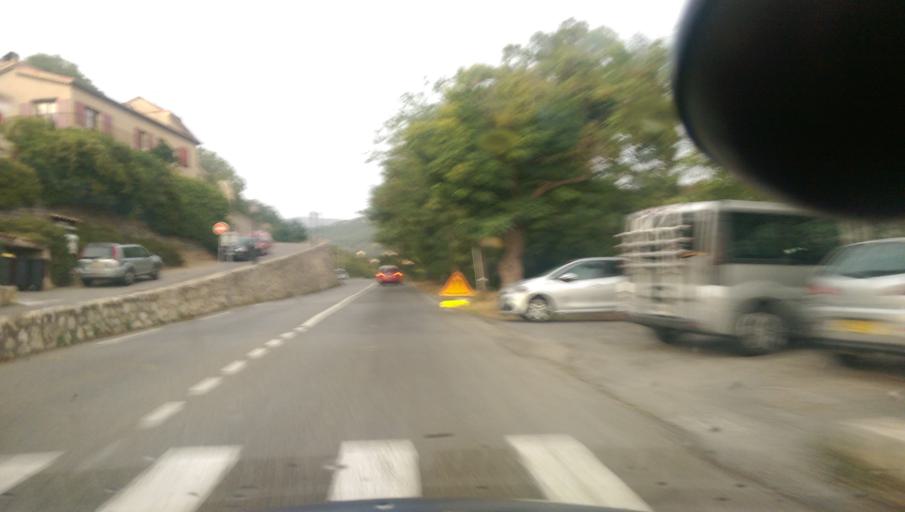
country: FR
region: Provence-Alpes-Cote d'Azur
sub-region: Departement des Alpes-Maritimes
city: Opio
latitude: 43.6747
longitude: 6.9779
